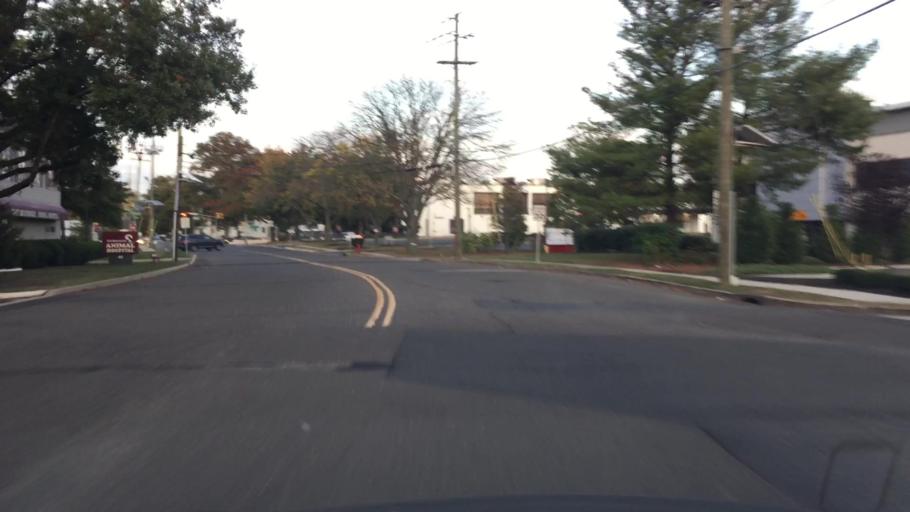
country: US
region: New Jersey
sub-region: Middlesex County
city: South River
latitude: 40.4333
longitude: -74.3902
